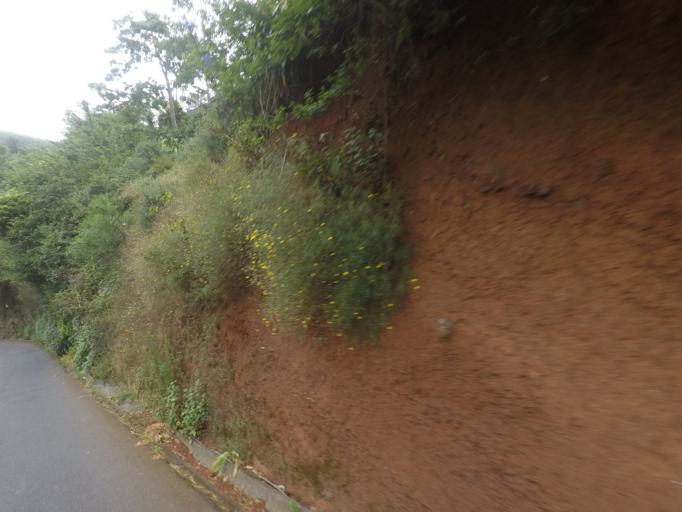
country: PT
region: Madeira
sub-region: Funchal
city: Nossa Senhora do Monte
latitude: 32.6647
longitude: -16.8720
